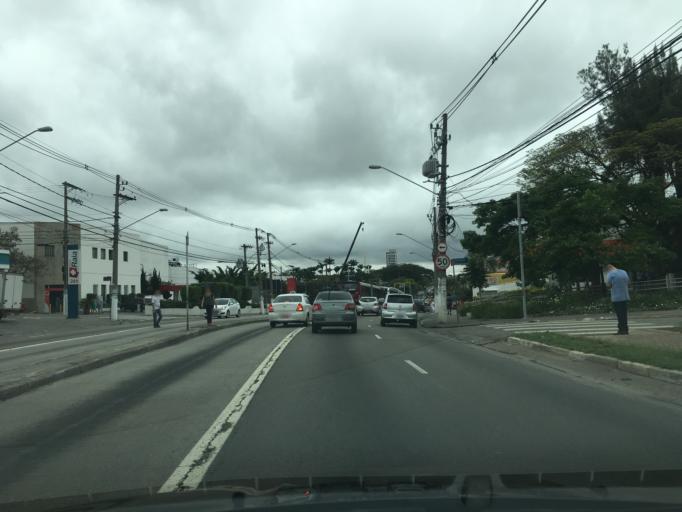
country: BR
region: Sao Paulo
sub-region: Taboao Da Serra
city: Taboao da Serra
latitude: -23.5874
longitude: -46.7262
